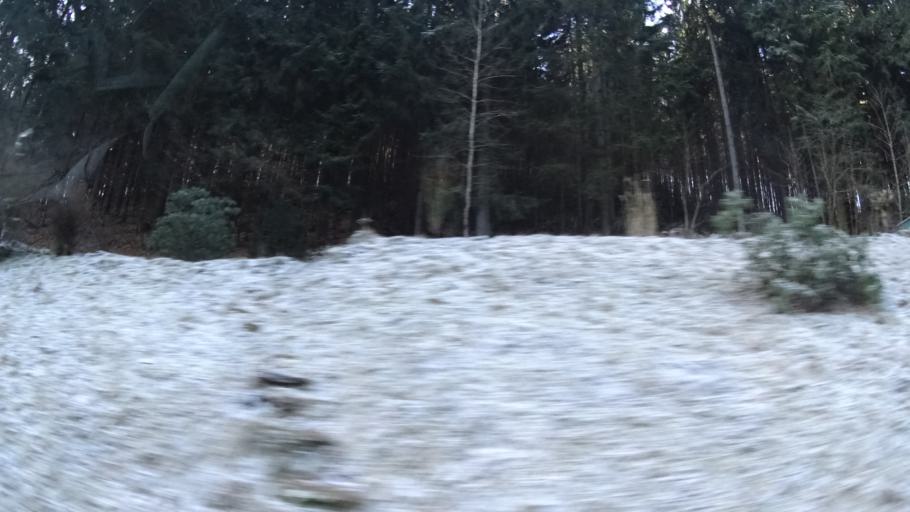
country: DE
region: Thuringia
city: Judenbach
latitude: 50.3758
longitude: 11.2179
